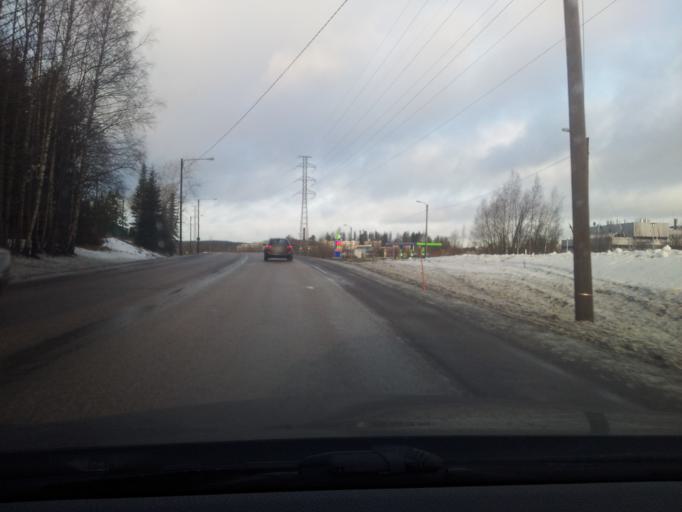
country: FI
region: Uusimaa
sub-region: Helsinki
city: Espoo
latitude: 60.1835
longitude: 24.6039
